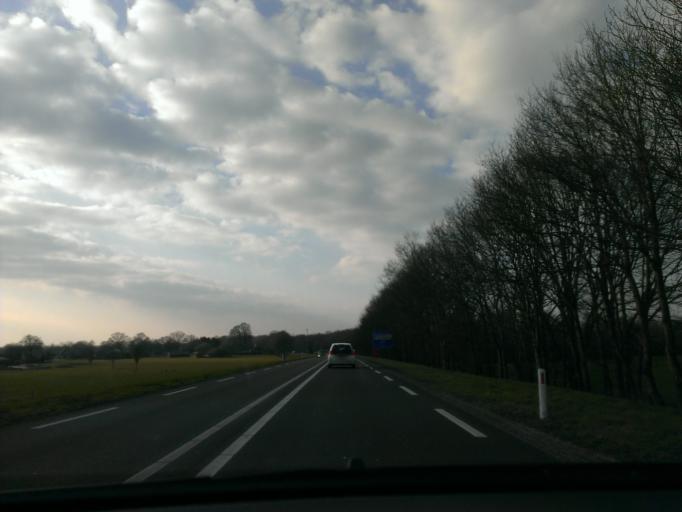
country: NL
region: Overijssel
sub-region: Gemeente Wierden
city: Wierden
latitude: 52.3565
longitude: 6.5727
